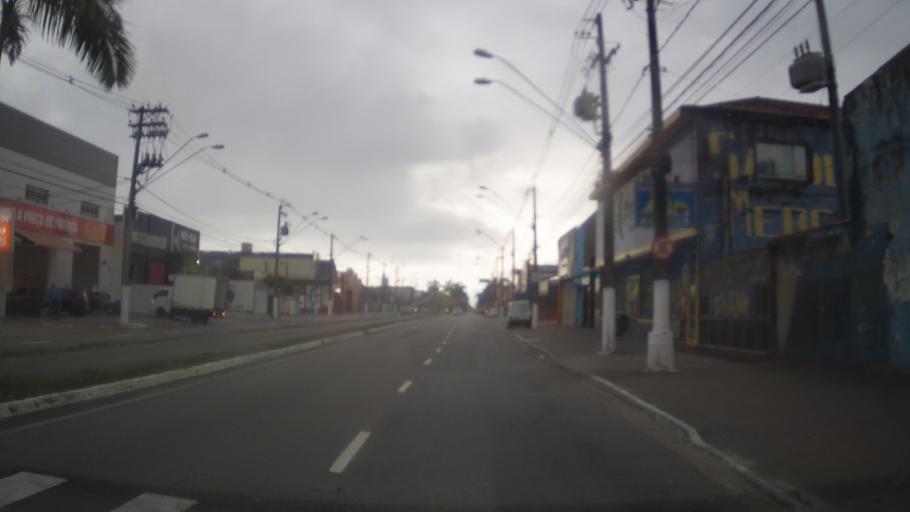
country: BR
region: Sao Paulo
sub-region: Praia Grande
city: Praia Grande
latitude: -24.0118
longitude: -46.4419
